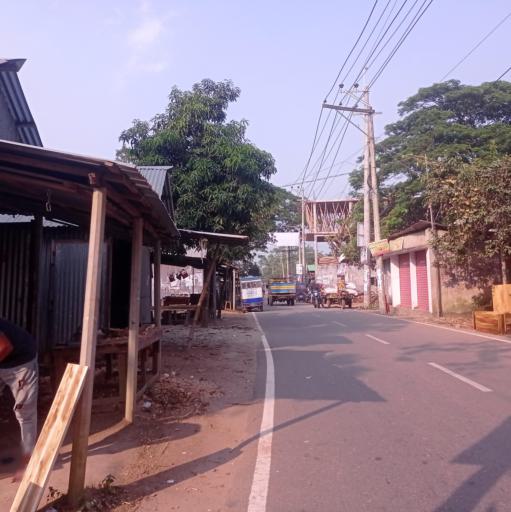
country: BD
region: Dhaka
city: Bhairab Bazar
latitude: 24.0803
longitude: 90.8489
